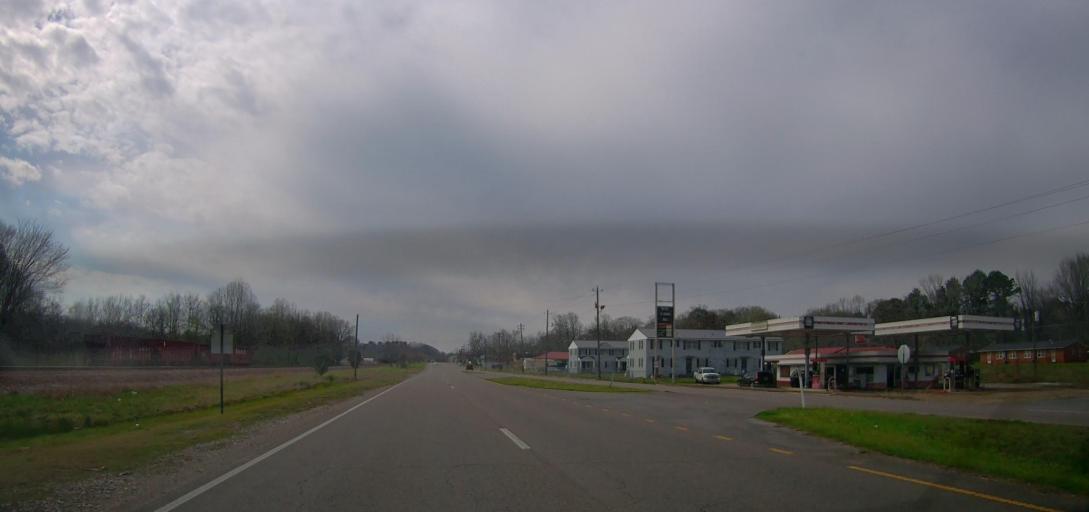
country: US
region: Alabama
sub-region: Walker County
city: Carbon Hill
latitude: 33.8861
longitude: -87.5224
